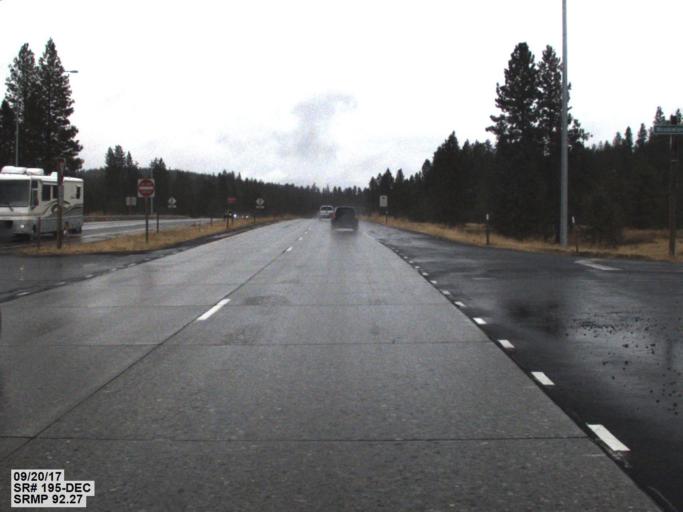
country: US
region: Washington
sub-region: Spokane County
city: Spokane
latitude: 47.6018
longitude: -117.4119
